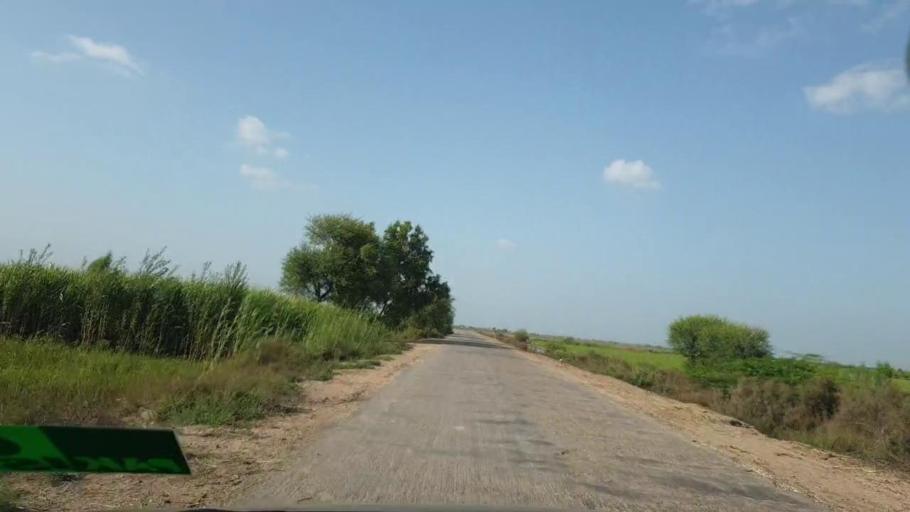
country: PK
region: Sindh
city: Tando Bago
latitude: 24.7228
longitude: 69.1958
